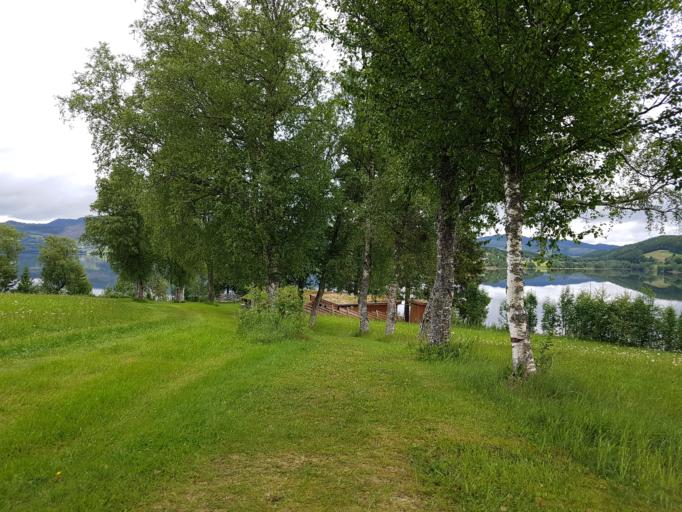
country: NO
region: Sor-Trondelag
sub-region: Selbu
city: Mebonden
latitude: 63.2345
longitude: 11.0289
